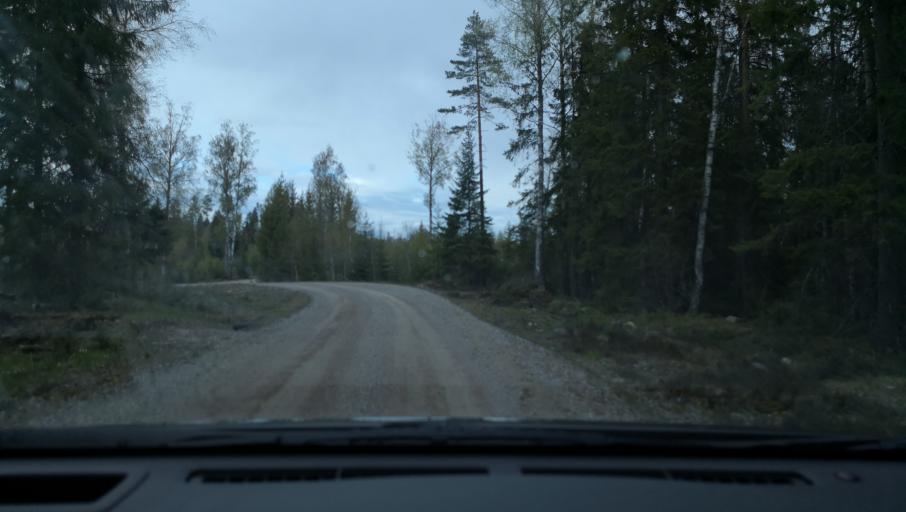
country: SE
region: Dalarna
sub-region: Saters Kommun
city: Saeter
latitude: 60.1961
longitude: 15.7416
